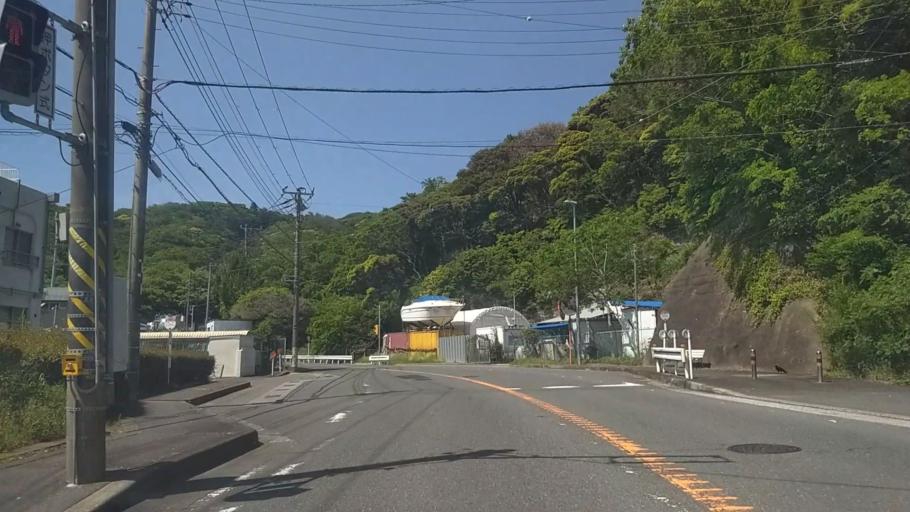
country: JP
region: Kanagawa
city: Zushi
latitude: 35.3121
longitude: 139.6008
